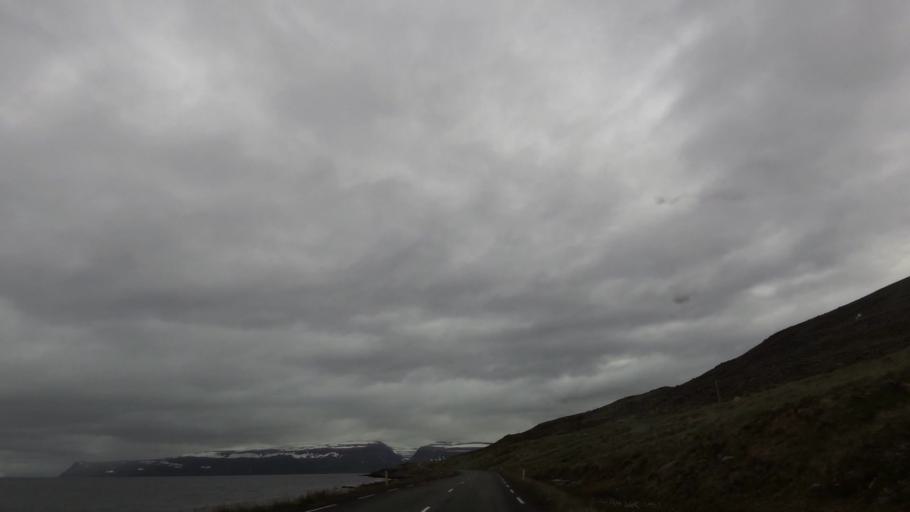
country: IS
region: Westfjords
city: Isafjoerdur
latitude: 66.0388
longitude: -22.7727
